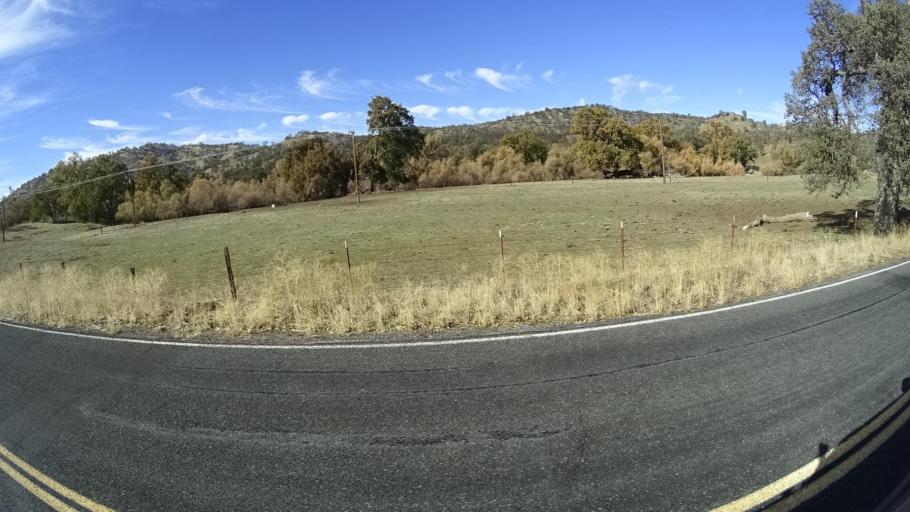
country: US
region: California
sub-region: Kern County
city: Alta Sierra
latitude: 35.6814
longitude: -118.7325
